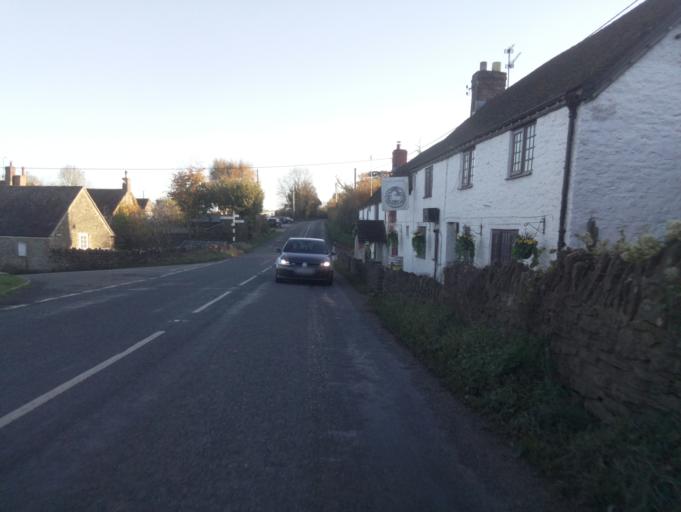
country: GB
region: England
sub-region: Somerset
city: Wincanton
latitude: 51.0210
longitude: -2.4392
